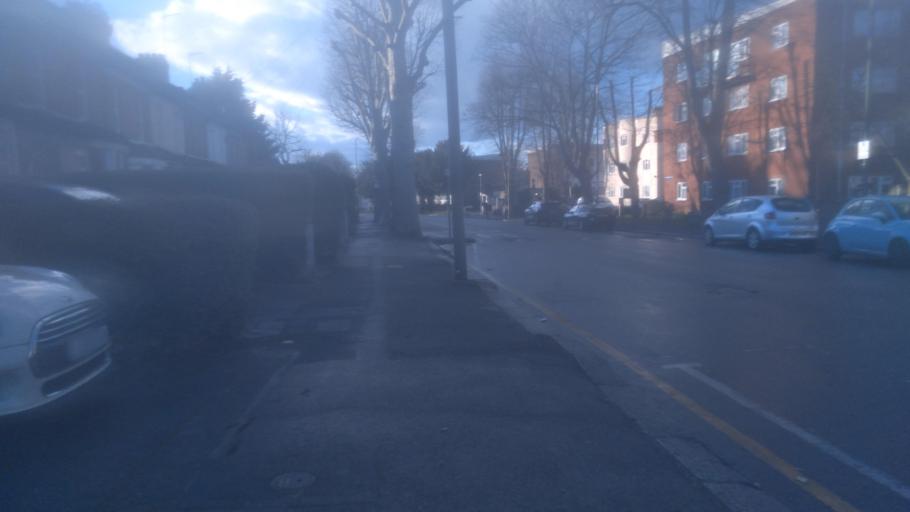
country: GB
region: England
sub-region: Greater London
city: Carshalton
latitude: 51.3663
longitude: -0.1878
